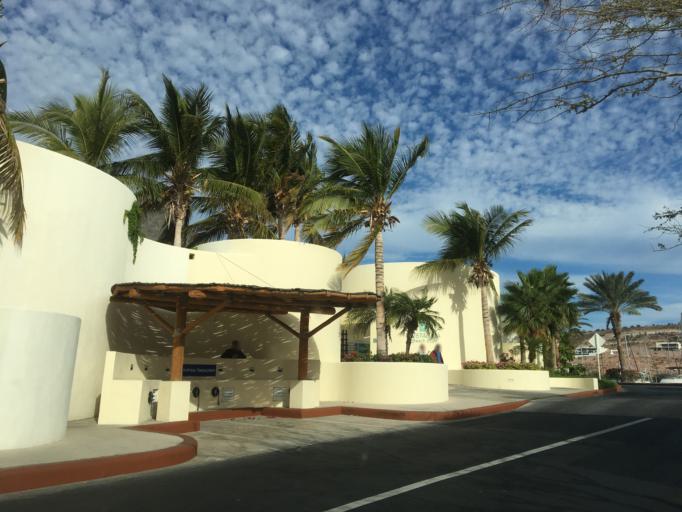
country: MX
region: Baja California Sur
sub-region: La Paz
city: La Paz
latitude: 24.2145
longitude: -110.2996
